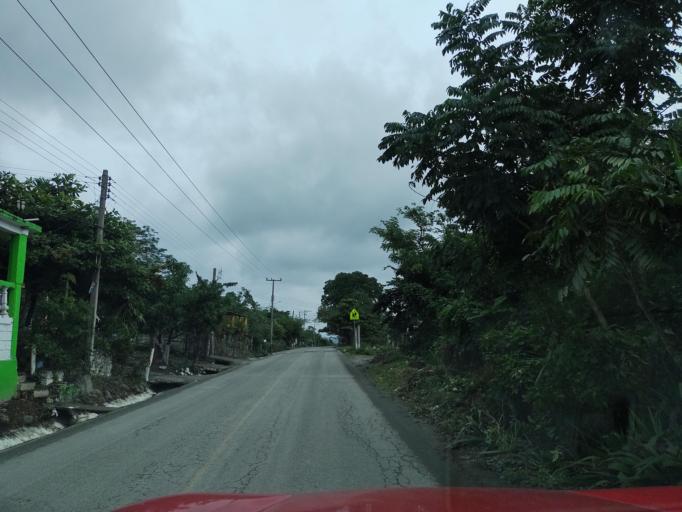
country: MX
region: Puebla
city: Espinal
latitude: 20.2628
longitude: -97.3541
